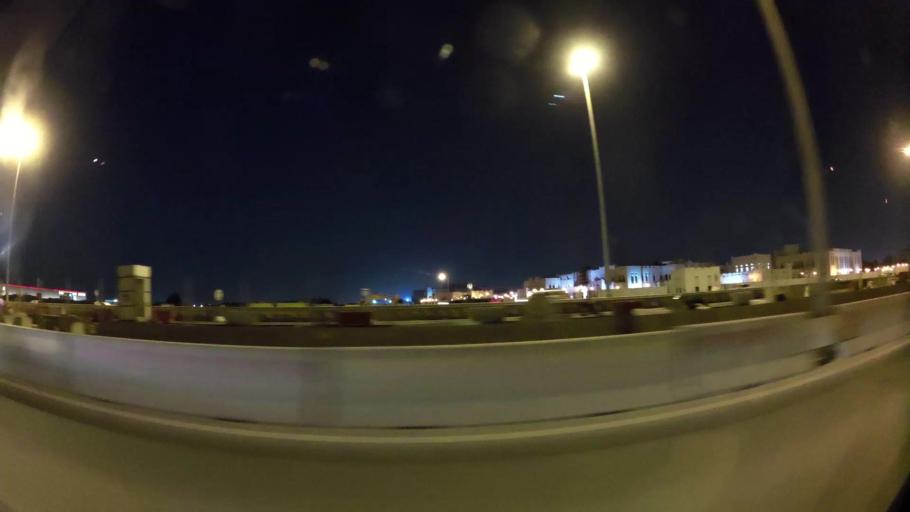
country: QA
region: Baladiyat ar Rayyan
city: Ar Rayyan
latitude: 25.2991
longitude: 51.4341
